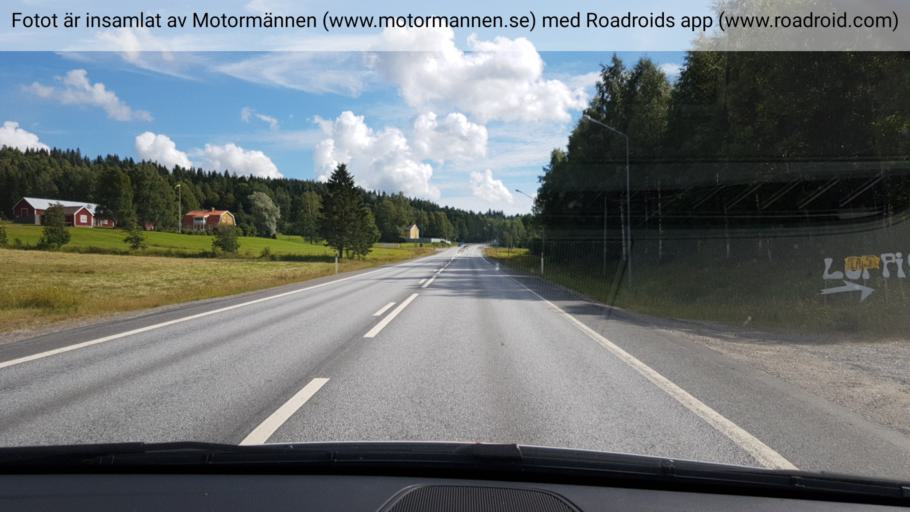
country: SE
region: Vaesterbotten
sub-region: Vannas Kommun
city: Vannasby
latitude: 63.9156
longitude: 19.8793
